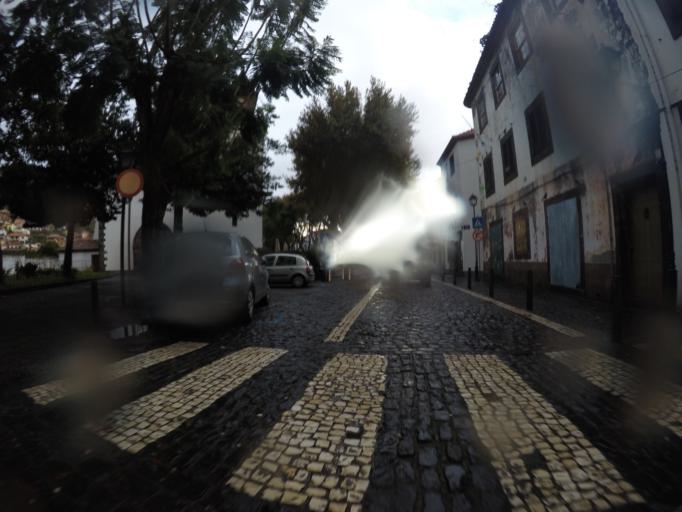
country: PT
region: Madeira
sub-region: Machico
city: Machico
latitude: 32.7187
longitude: -16.7666
